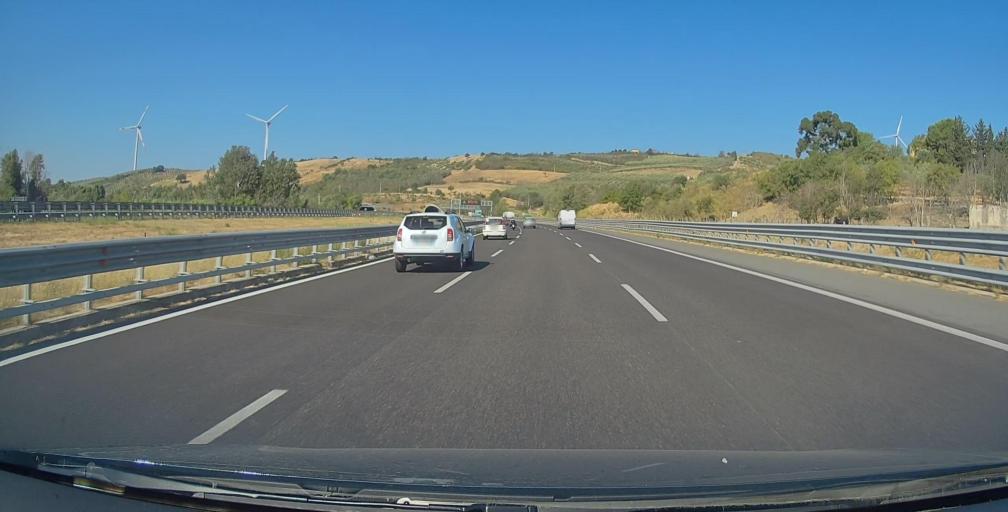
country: IT
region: Campania
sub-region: Provincia di Salerno
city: Serre
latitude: 40.6271
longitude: 15.1855
